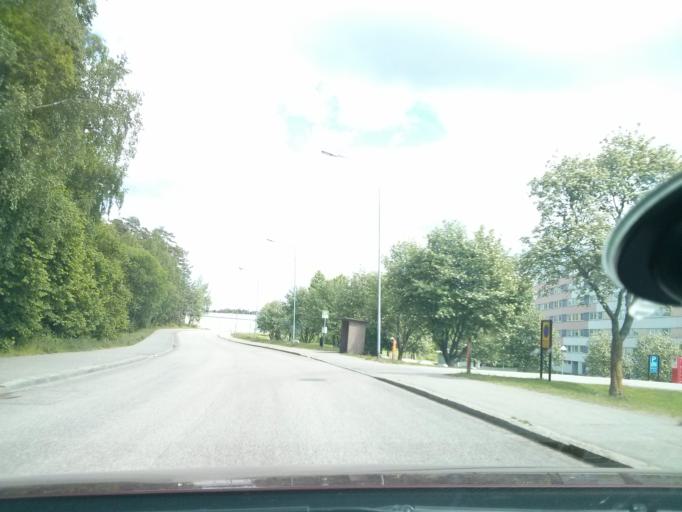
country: SE
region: Soedermanland
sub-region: Nykopings Kommun
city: Nykoping
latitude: 58.7689
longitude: 17.0122
